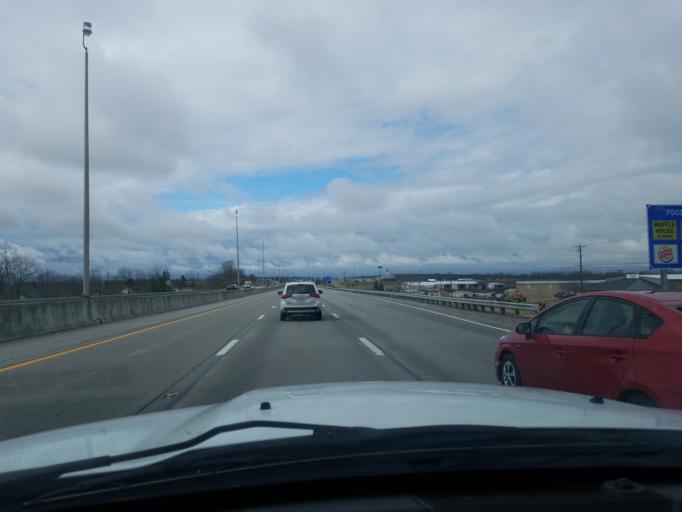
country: US
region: Kentucky
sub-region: Clark County
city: Winchester
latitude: 38.0083
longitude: -84.1993
